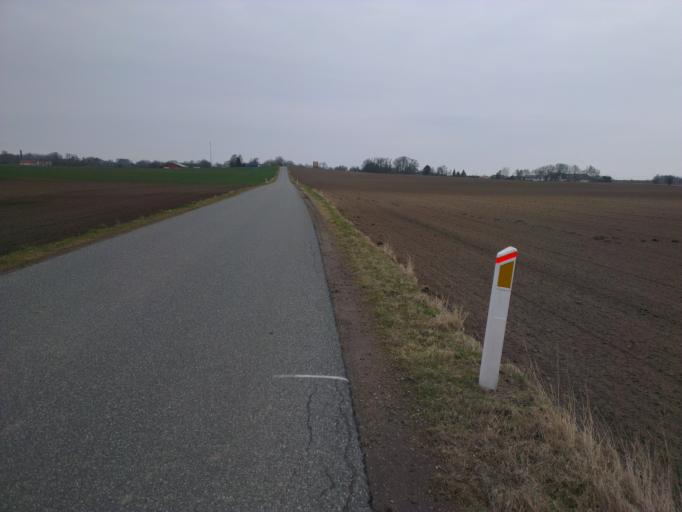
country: DK
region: Capital Region
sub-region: Frederikssund Kommune
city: Skibby
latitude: 55.7523
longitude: 11.9093
